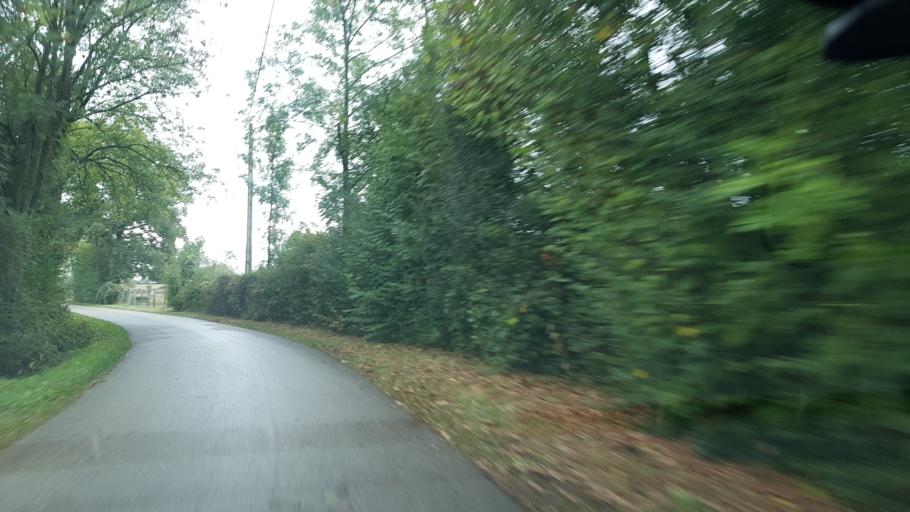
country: FR
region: Rhone-Alpes
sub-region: Departement de l'Ain
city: Tossiat
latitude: 46.1346
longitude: 5.3151
